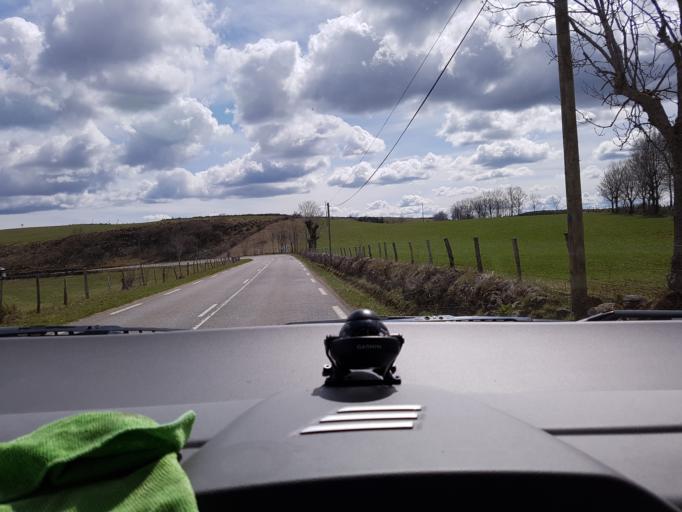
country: FR
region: Midi-Pyrenees
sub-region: Departement de l'Aveyron
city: Laguiole
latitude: 44.7073
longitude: 2.8582
